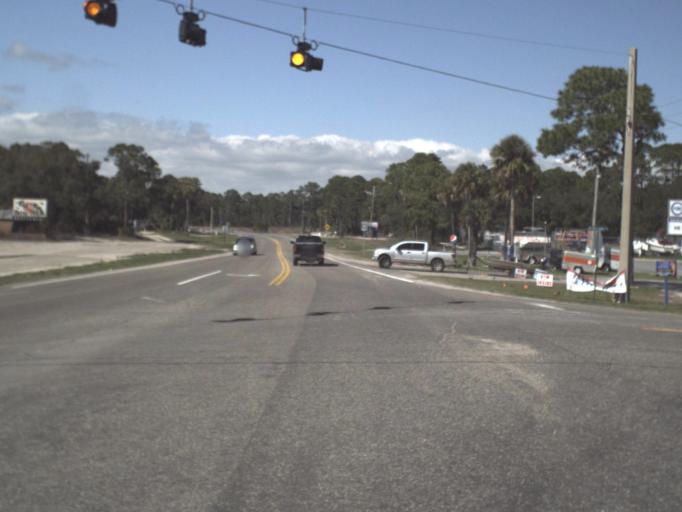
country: US
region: Florida
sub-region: Wakulla County
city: Crawfordville
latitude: 29.9785
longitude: -84.3832
